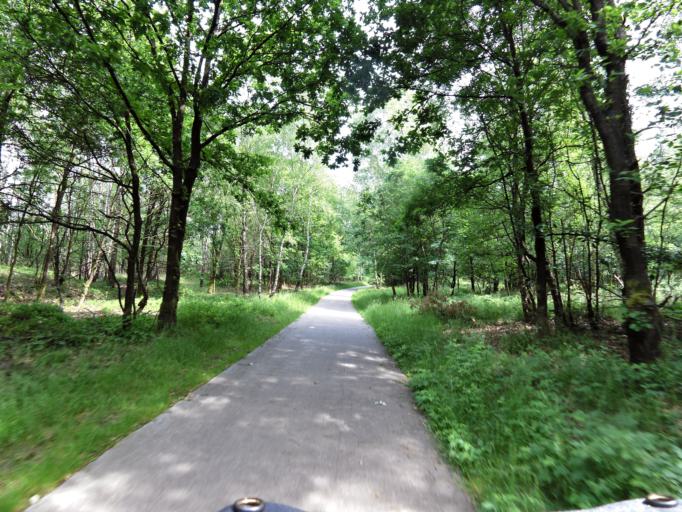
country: NL
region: Gelderland
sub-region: Gemeente Rozendaal
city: Rozendaal
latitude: 52.0256
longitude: 5.9916
